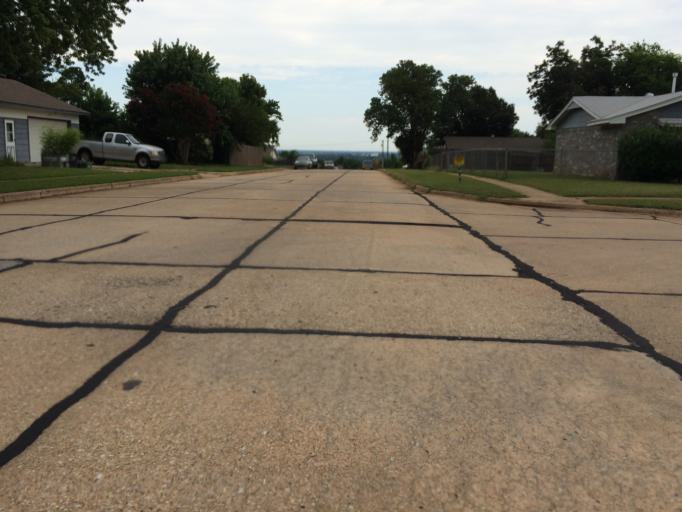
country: US
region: Oklahoma
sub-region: Cleveland County
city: Hall Park
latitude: 35.2529
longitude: -97.4191
